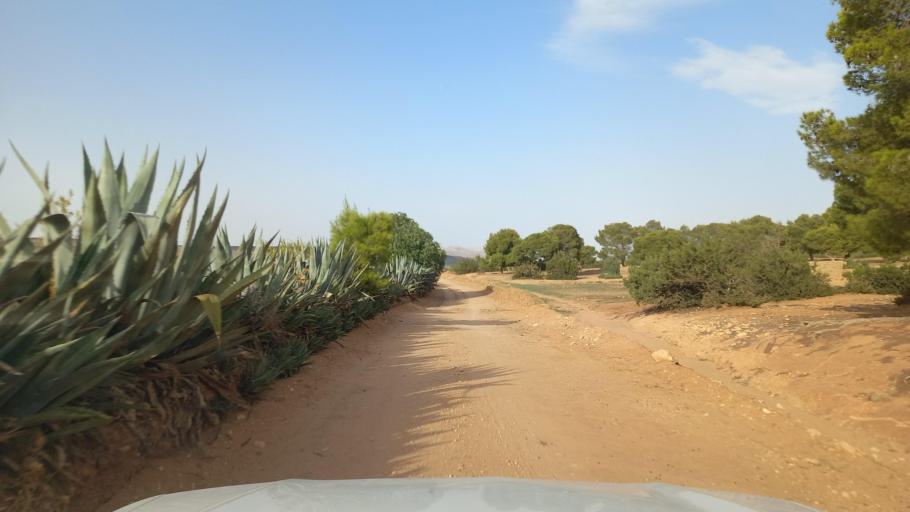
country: TN
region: Al Qasrayn
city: Kasserine
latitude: 35.3462
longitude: 8.8647
